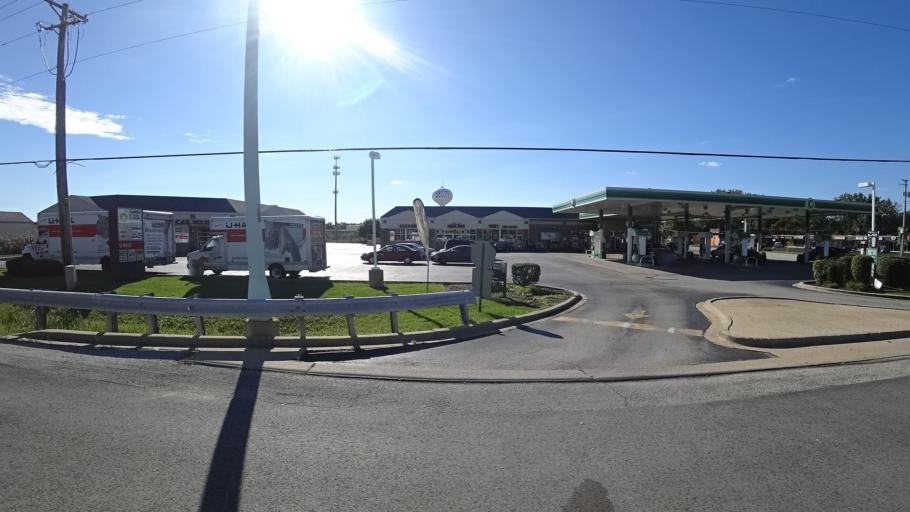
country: US
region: Illinois
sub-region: Cook County
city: Country Club Hills
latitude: 41.5565
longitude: -87.7332
